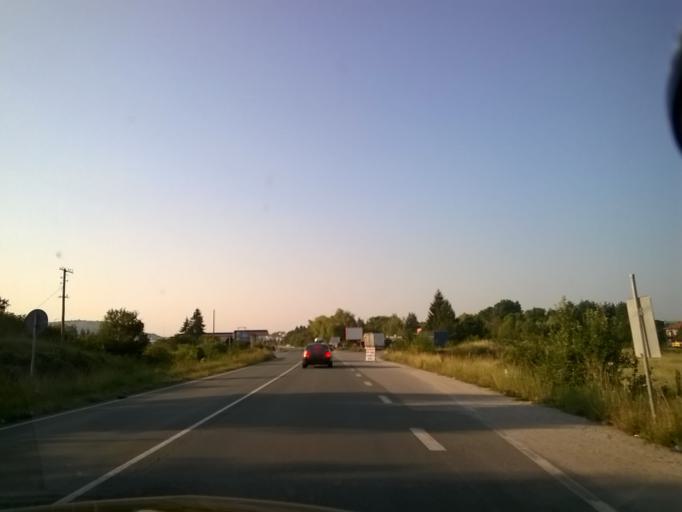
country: BG
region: Sofiya
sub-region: Obshtina Dragoman
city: Dragoman
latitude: 42.9237
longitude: 22.9366
